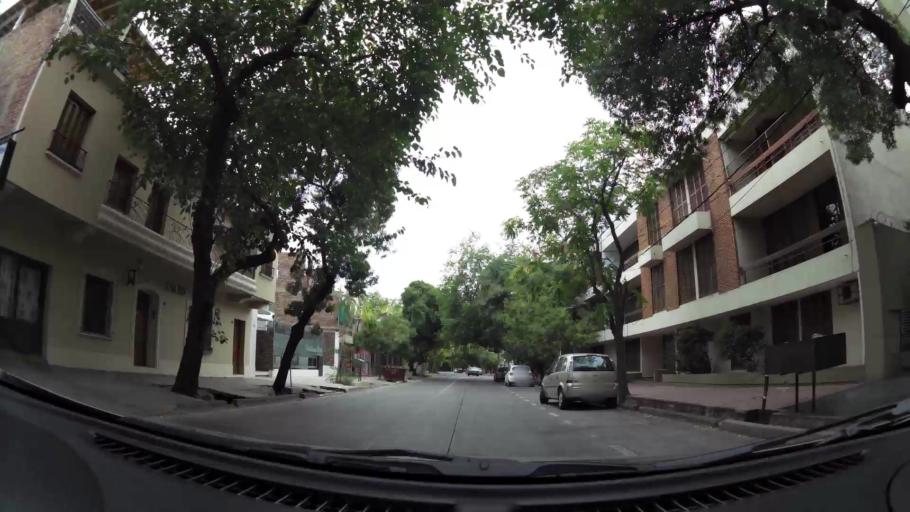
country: AR
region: Mendoza
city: Mendoza
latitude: -32.8954
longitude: -68.8591
